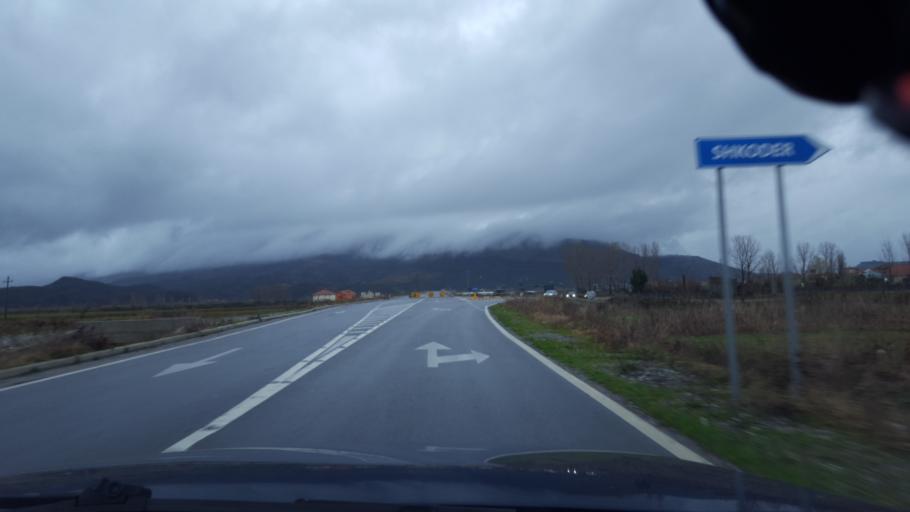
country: AL
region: Shkoder
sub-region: Rrethi i Shkodres
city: Berdica e Madhe
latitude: 42.0048
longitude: 19.4798
